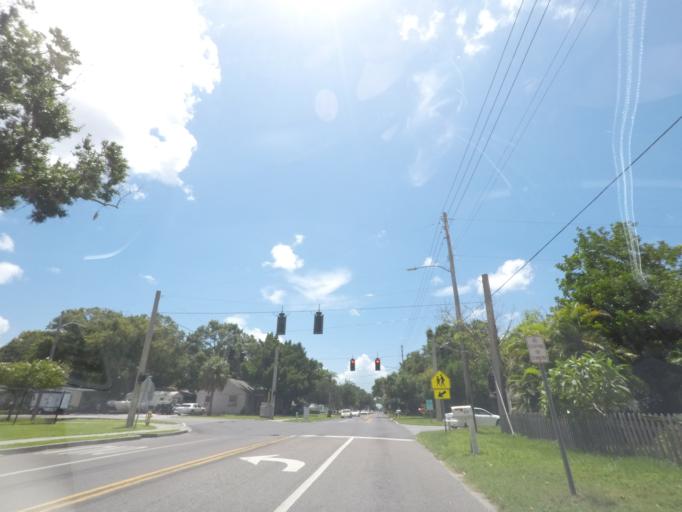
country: US
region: Florida
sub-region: Pinellas County
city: Gulfport
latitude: 27.7595
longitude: -82.7121
